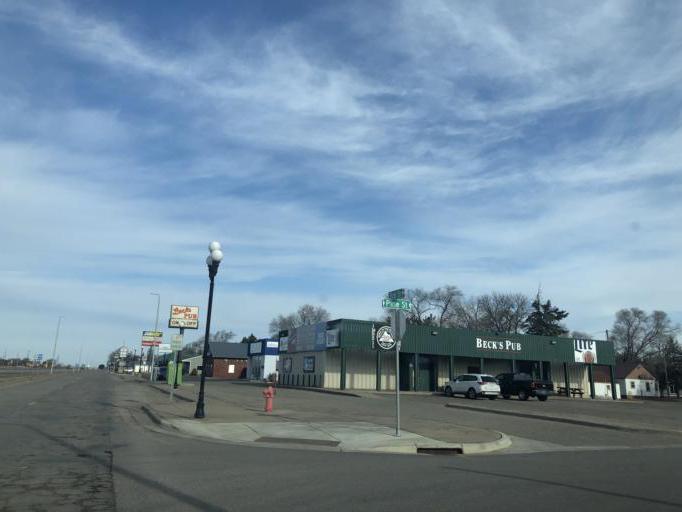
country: US
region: Minnesota
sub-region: Sherburne County
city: Becker
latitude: 45.3898
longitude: -93.8716
